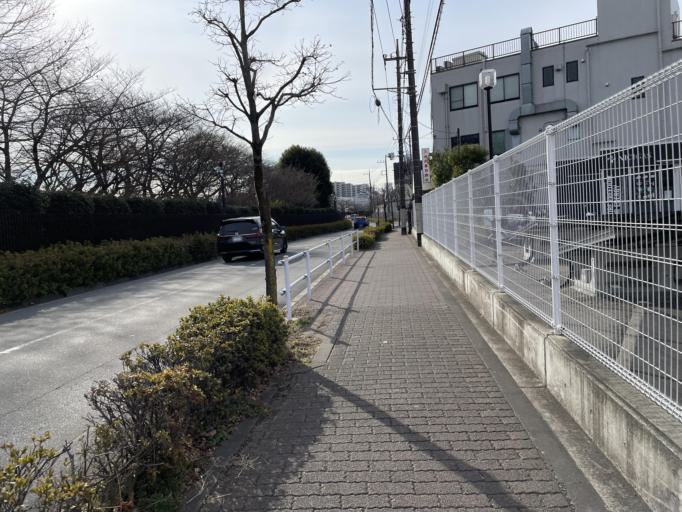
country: JP
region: Tokyo
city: Kokubunji
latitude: 35.6843
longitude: 139.4608
